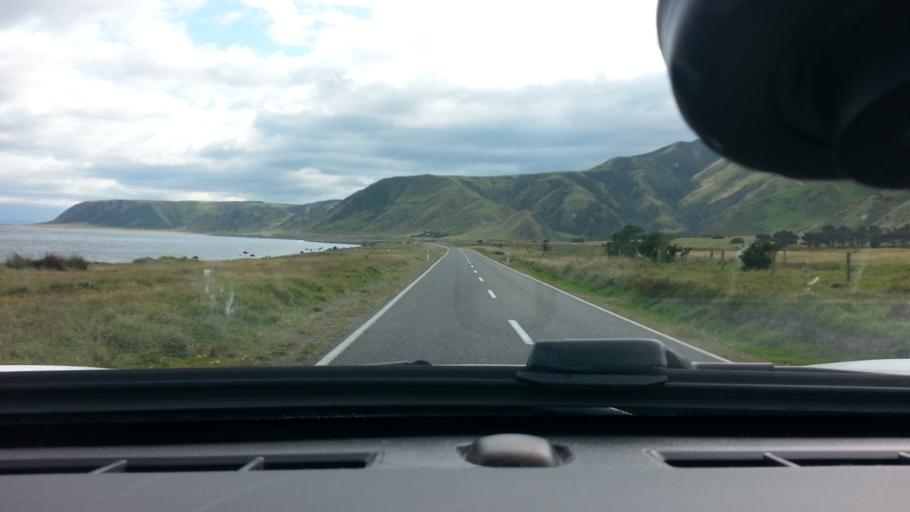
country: NZ
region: Wellington
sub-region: South Wairarapa District
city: Waipawa
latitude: -41.5605
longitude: 175.2218
